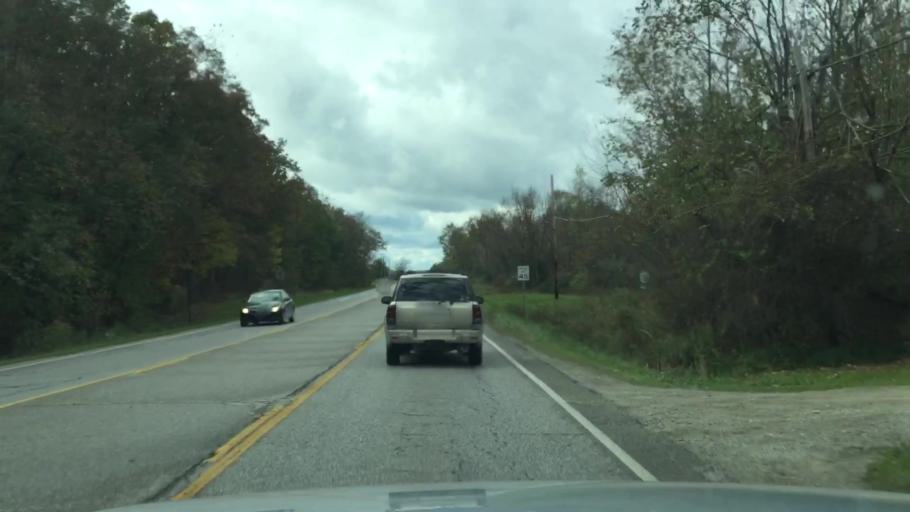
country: US
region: Michigan
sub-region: Lapeer County
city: Lapeer
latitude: 43.0486
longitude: -83.3495
